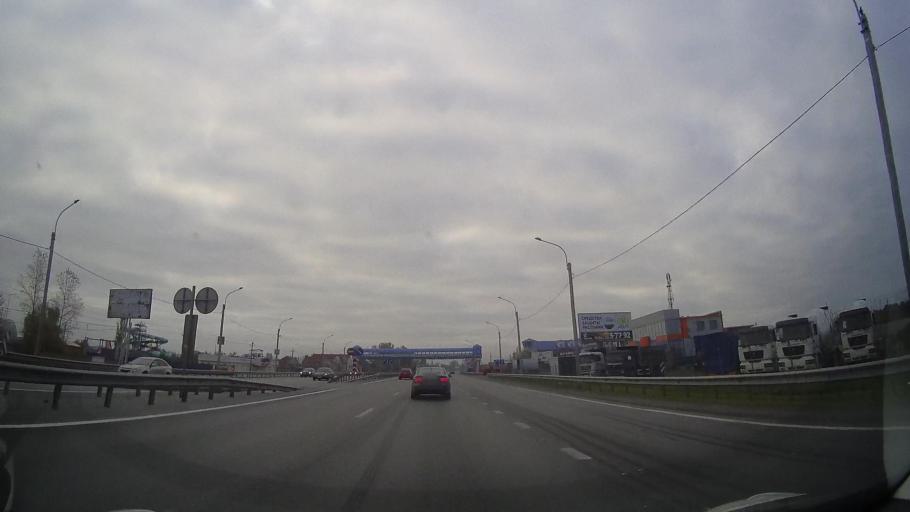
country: RU
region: Rostov
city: Bataysk
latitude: 47.1562
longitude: 39.7686
